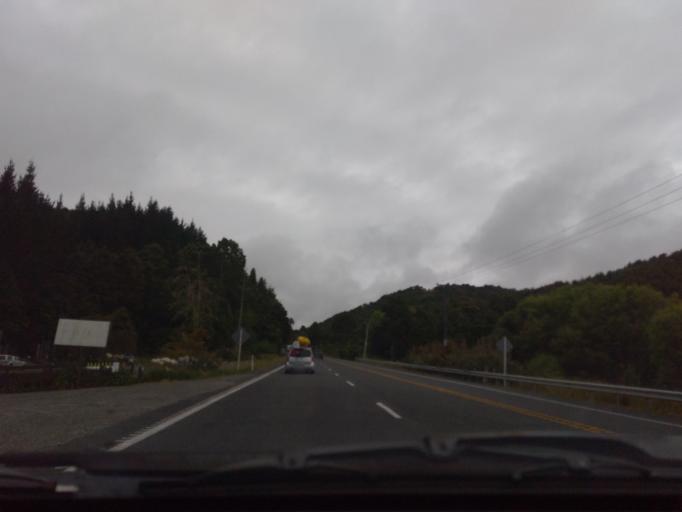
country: NZ
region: Auckland
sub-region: Auckland
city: Wellsford
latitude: -36.1204
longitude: 174.4359
